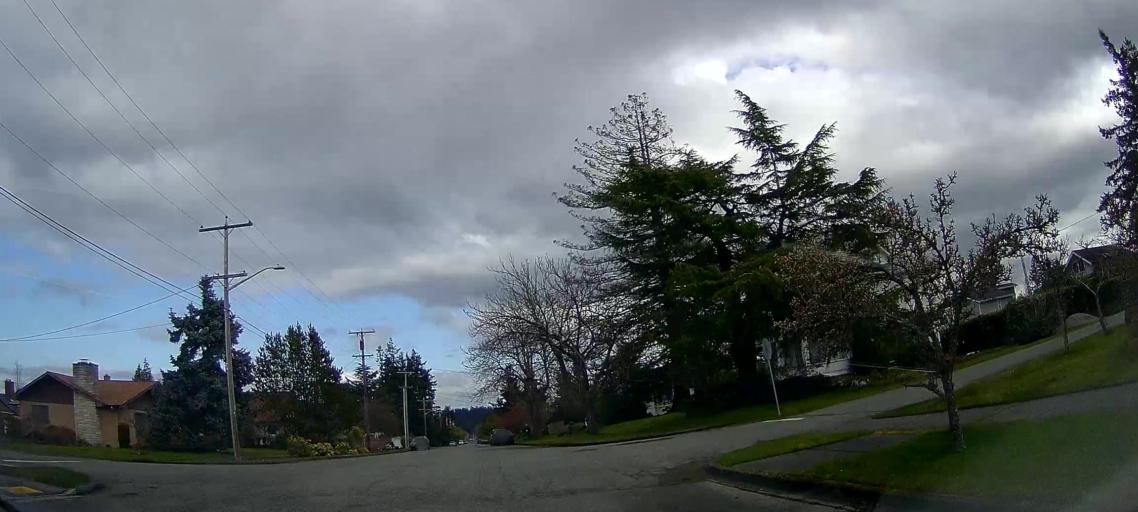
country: US
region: Washington
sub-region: Skagit County
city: Anacortes
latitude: 48.5151
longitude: -122.6269
